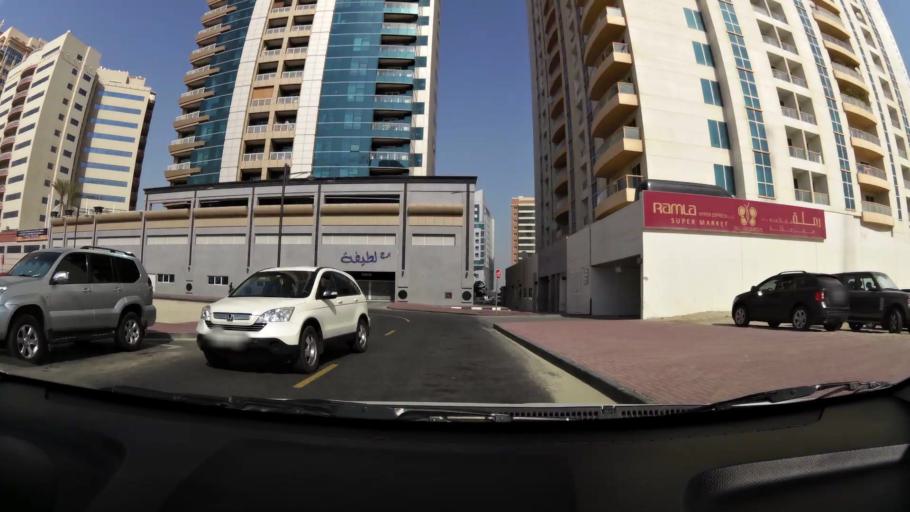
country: AE
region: Ash Shariqah
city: Sharjah
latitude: 25.2968
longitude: 55.3630
